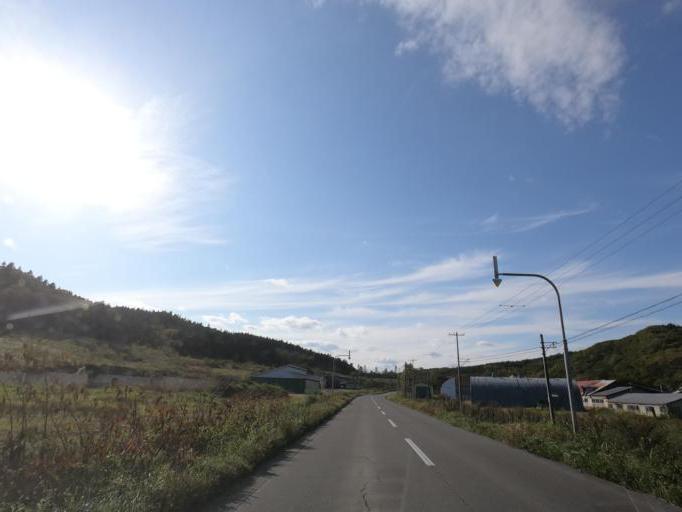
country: JP
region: Hokkaido
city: Obihiro
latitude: 42.6170
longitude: 143.4137
